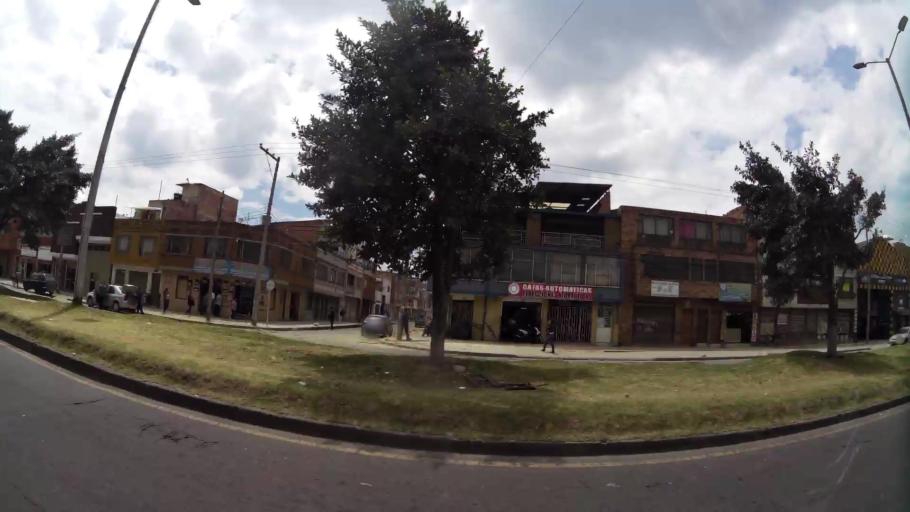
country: CO
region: Bogota D.C.
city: Bogota
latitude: 4.5921
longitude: -74.1062
